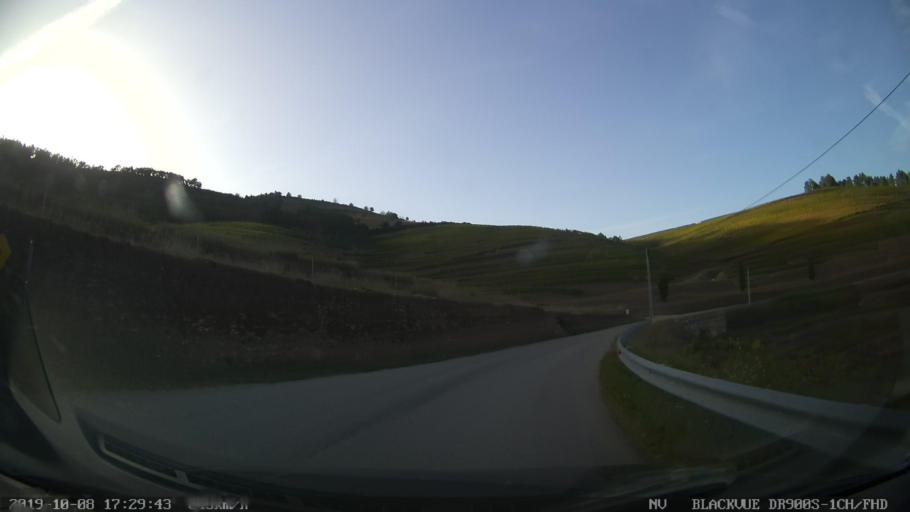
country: PT
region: Vila Real
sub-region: Sabrosa
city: Vilela
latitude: 41.2335
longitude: -7.5721
